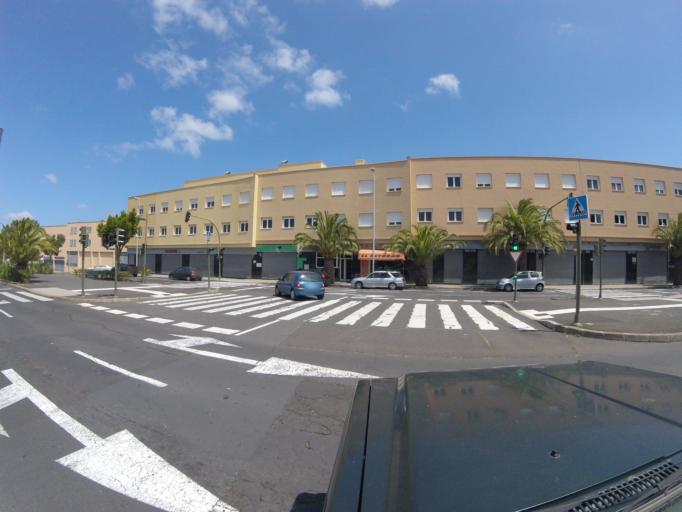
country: ES
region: Canary Islands
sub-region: Provincia de Santa Cruz de Tenerife
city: La Laguna
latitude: 28.4435
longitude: -16.3116
